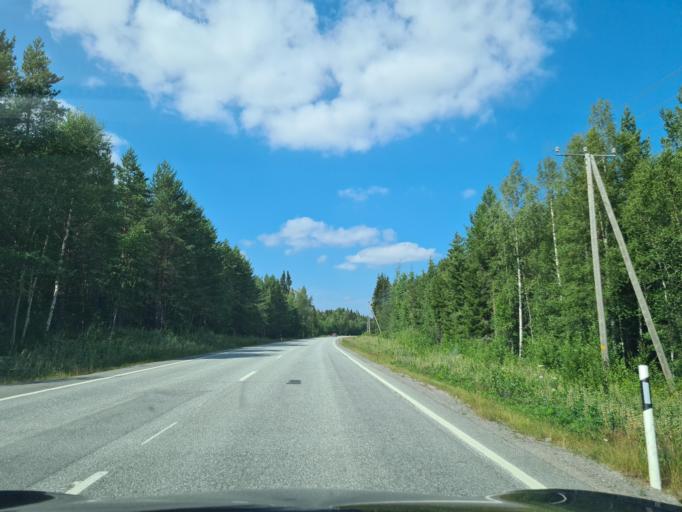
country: FI
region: Ostrobothnia
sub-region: Vaasa
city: Vaasa
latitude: 63.1713
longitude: 21.5825
